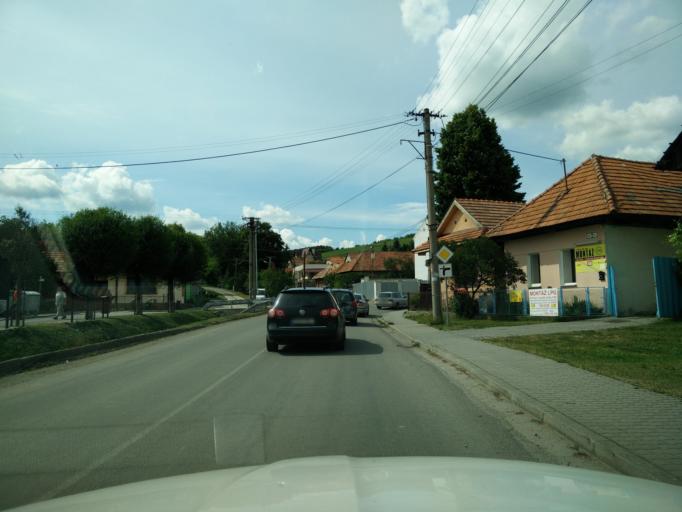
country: SK
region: Nitriansky
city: Bojnice
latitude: 48.7639
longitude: 18.5716
